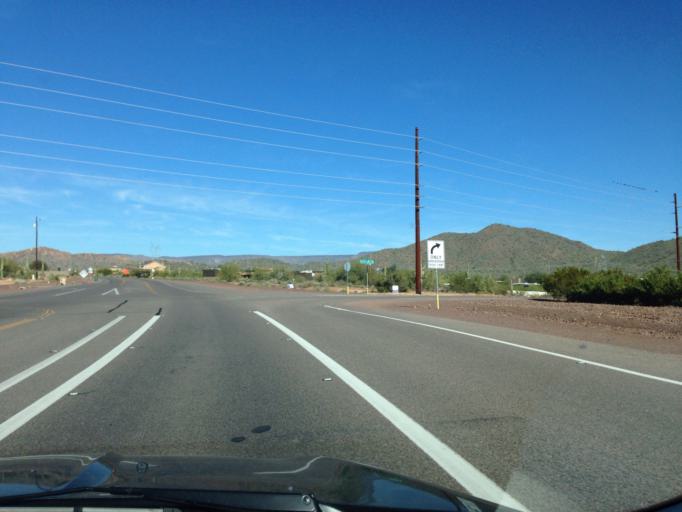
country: US
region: Arizona
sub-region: Maricopa County
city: Anthem
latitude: 33.8422
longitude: -112.0644
